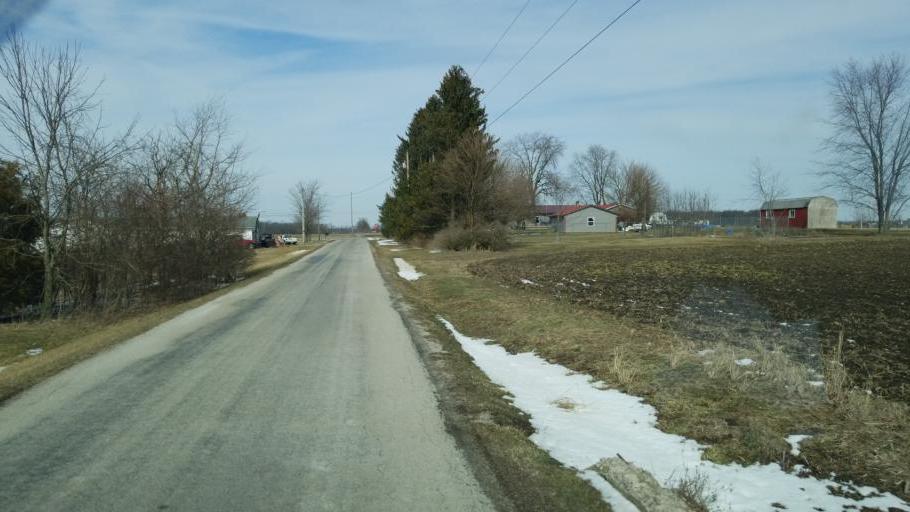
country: US
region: Ohio
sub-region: Delaware County
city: Ashley
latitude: 40.4068
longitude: -82.9352
